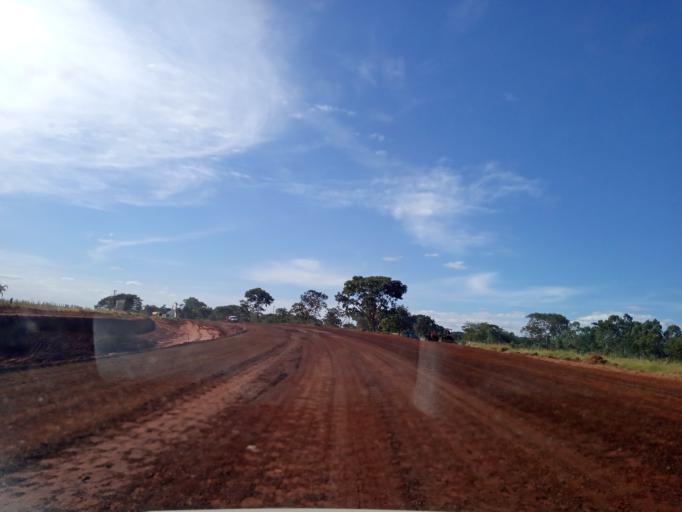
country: BR
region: Minas Gerais
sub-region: Ituiutaba
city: Ituiutaba
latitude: -18.9768
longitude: -49.5050
